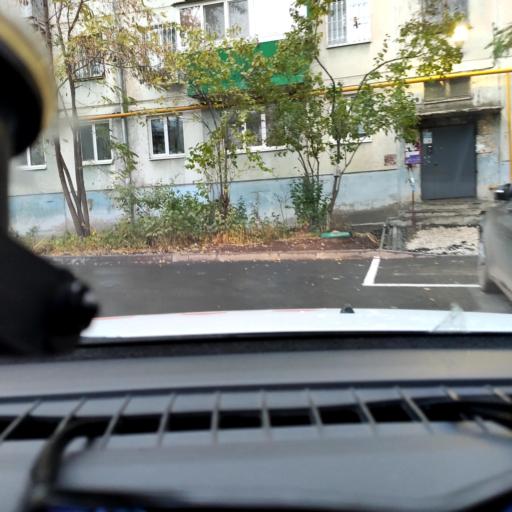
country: RU
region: Samara
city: Samara
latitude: 53.1875
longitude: 50.1755
